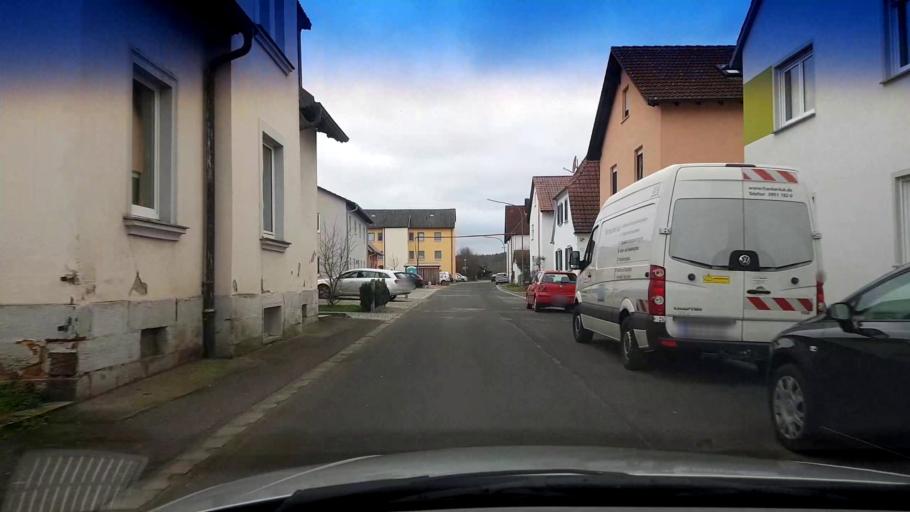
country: DE
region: Bavaria
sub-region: Upper Franconia
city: Baunach
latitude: 49.9823
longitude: 10.8461
